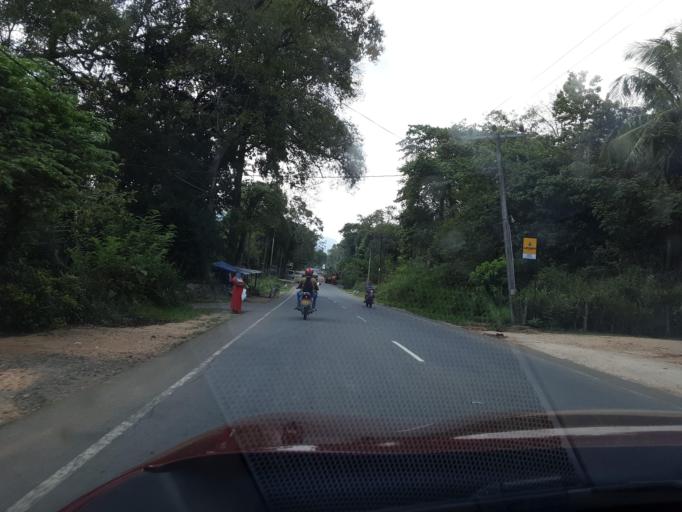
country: LK
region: Uva
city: Haputale
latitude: 6.6819
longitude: 81.1096
